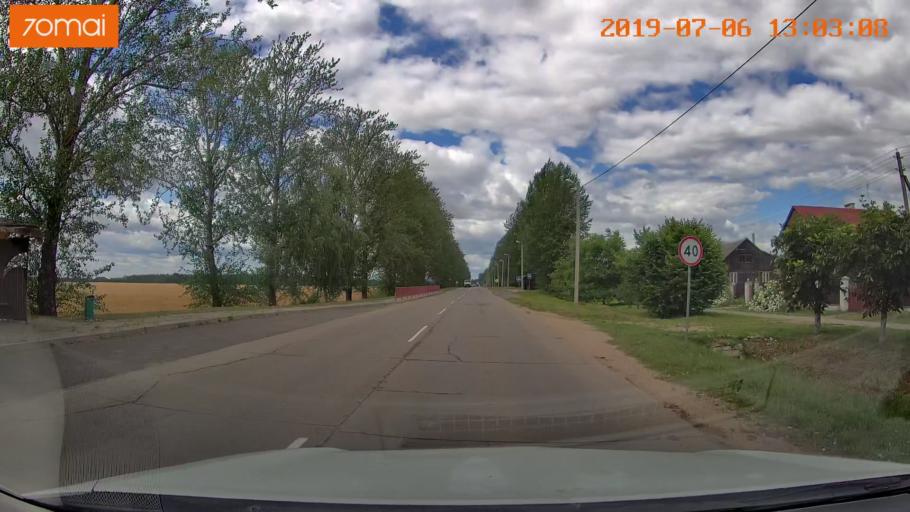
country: BY
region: Minsk
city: Dzyarzhynsk
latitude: 53.6882
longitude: 27.1064
